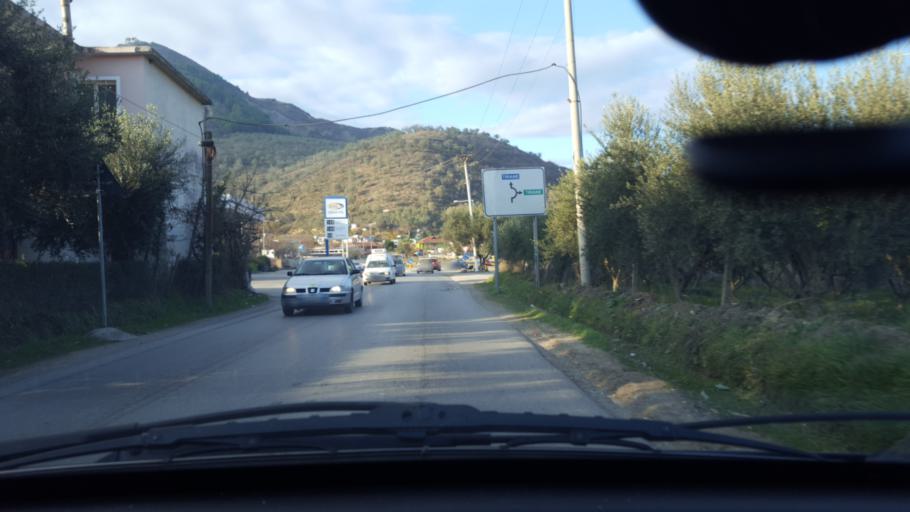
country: AL
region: Elbasan
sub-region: Rrethi i Elbasanit
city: Bradashesh
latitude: 41.1047
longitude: 20.0256
